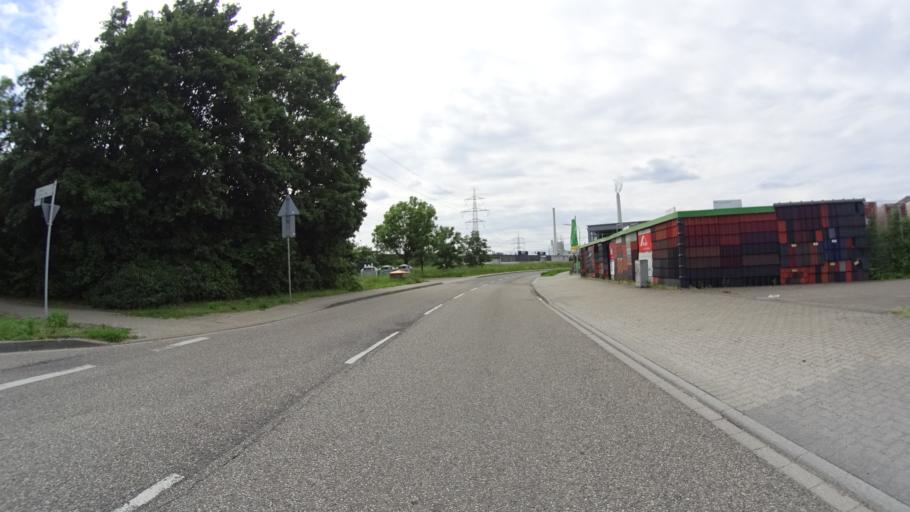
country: DE
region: Baden-Wuerttemberg
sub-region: Karlsruhe Region
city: Rheinstetten
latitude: 49.0081
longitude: 8.3260
